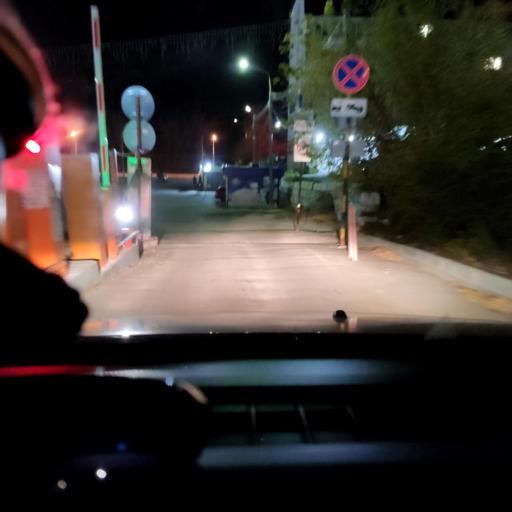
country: RU
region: Samara
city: Samara
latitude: 53.2126
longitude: 50.1838
